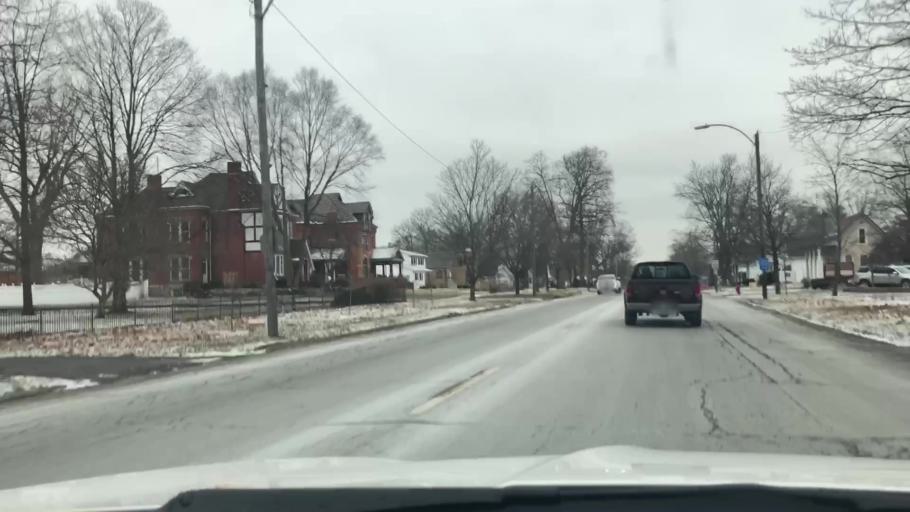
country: US
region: Indiana
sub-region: Fulton County
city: Rochester
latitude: 41.0590
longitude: -86.2166
